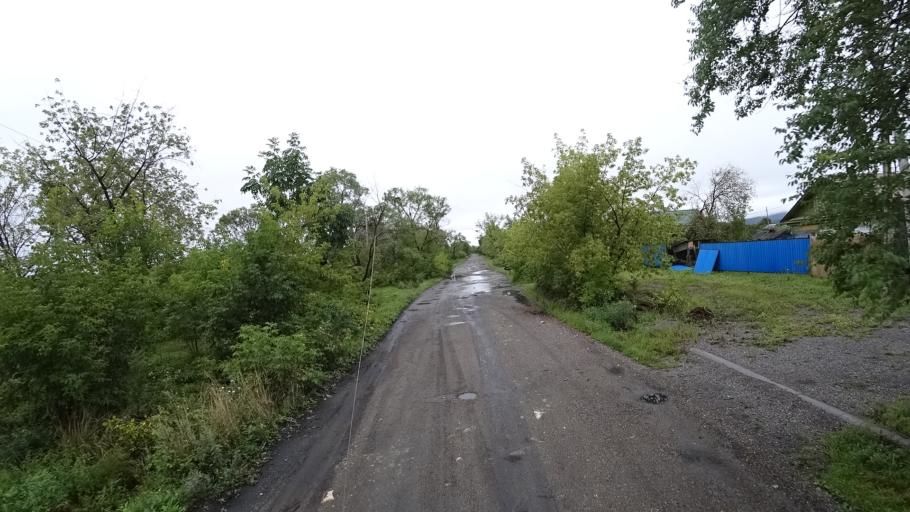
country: RU
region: Primorskiy
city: Monastyrishche
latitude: 44.1994
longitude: 132.4663
